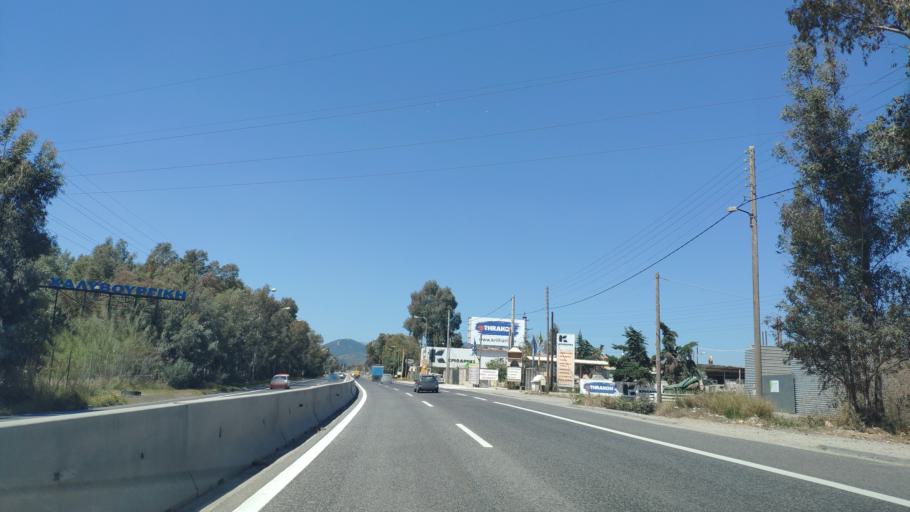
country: GR
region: Attica
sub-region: Nomarchia Dytikis Attikis
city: Aspropyrgos
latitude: 38.0496
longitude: 23.5690
